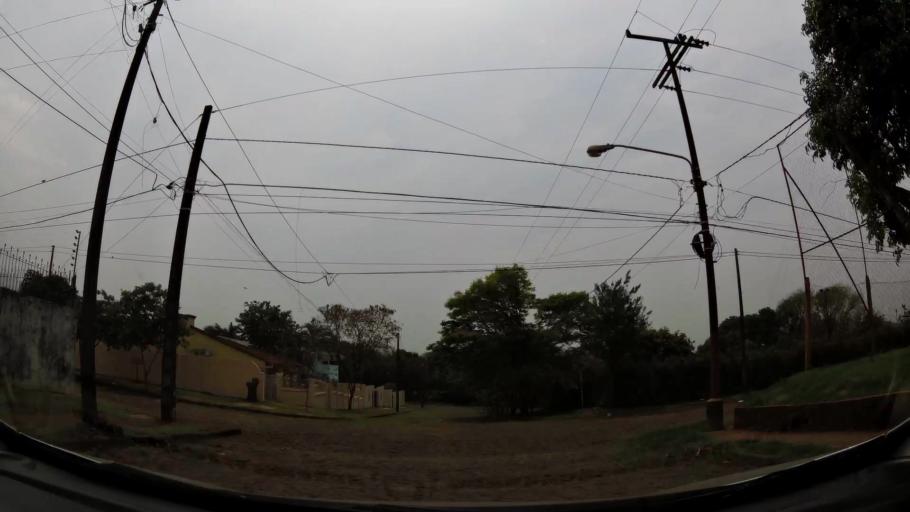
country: PY
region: Alto Parana
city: Presidente Franco
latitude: -25.5500
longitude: -54.6148
